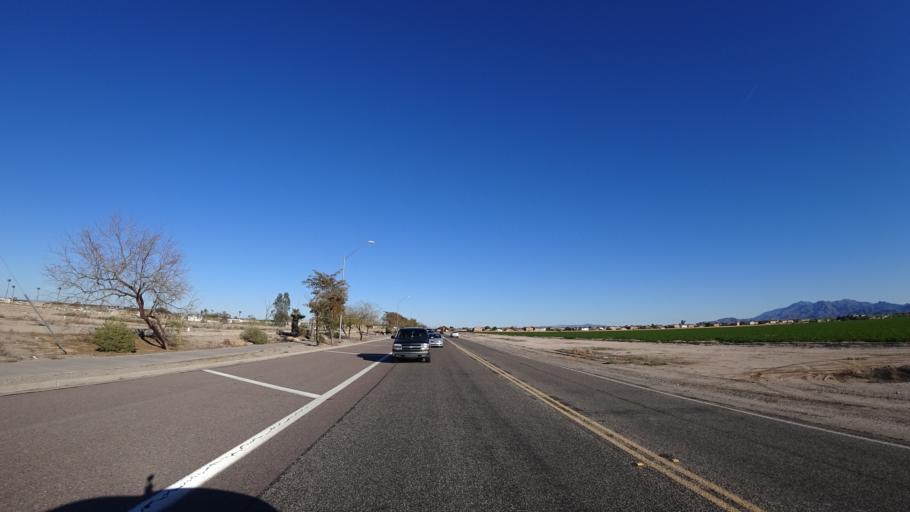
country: US
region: Arizona
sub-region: Maricopa County
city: Goodyear
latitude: 33.4502
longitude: -112.4410
